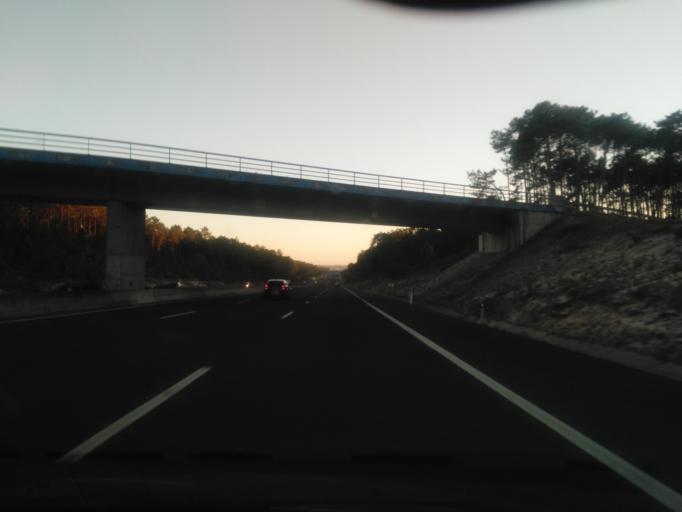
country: PT
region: Leiria
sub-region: Alcobaca
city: Pataias
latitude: 39.6562
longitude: -8.9607
